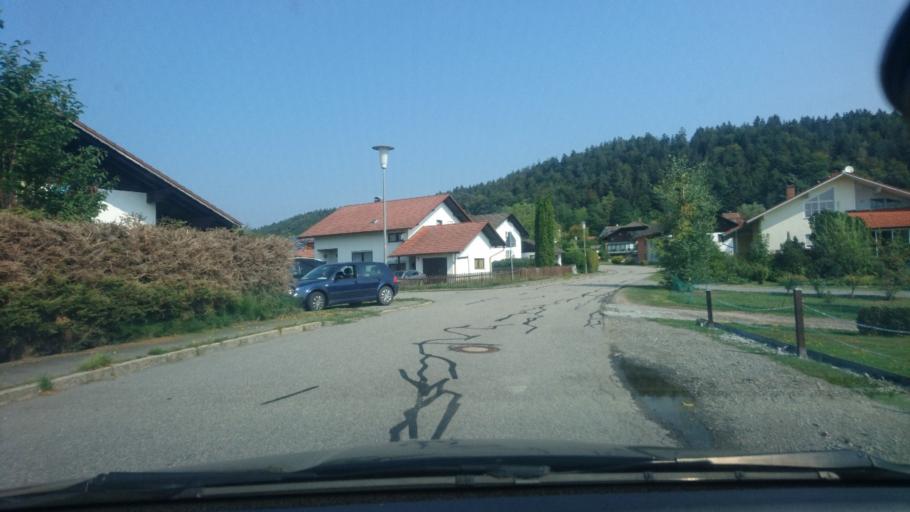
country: DE
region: Bavaria
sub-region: Lower Bavaria
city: Spiegelau
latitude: 48.9080
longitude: 13.3406
